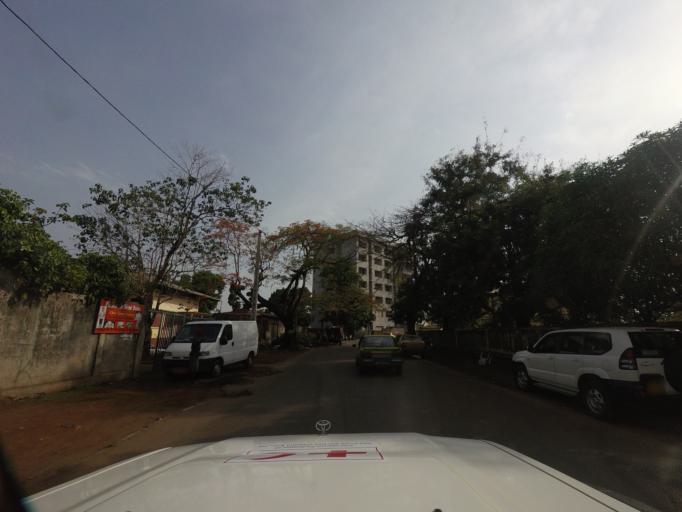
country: GN
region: Conakry
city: Camayenne
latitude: 9.5151
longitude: -13.6975
